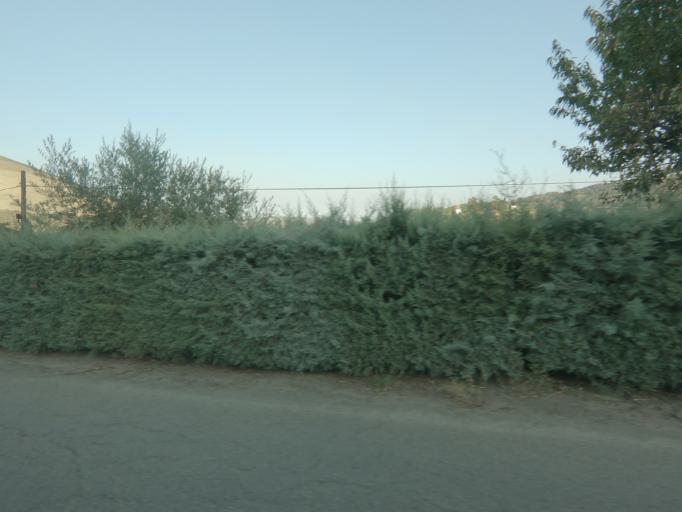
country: PT
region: Vila Real
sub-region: Sabrosa
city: Vilela
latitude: 41.1645
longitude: -7.6316
